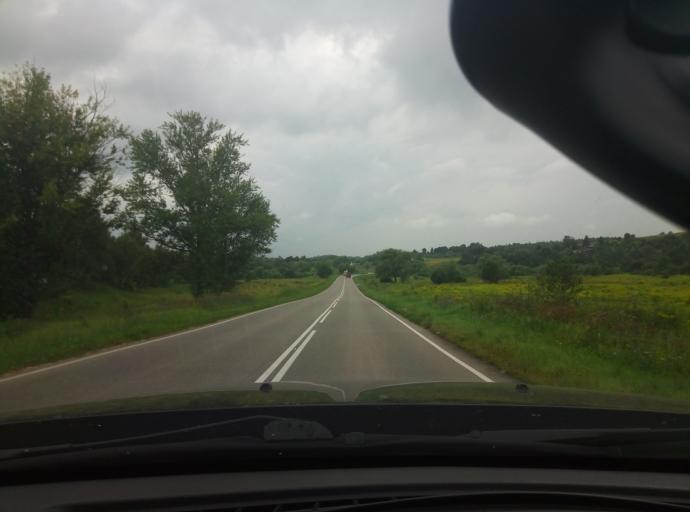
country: RU
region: Tula
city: Lomintsevskiy
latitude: 53.9613
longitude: 37.6535
